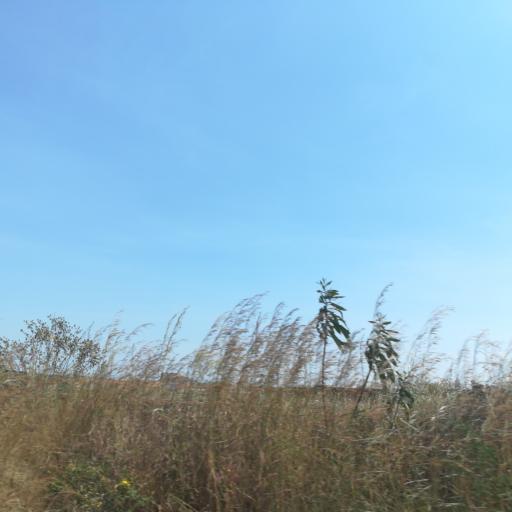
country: NG
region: Plateau
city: Bukuru
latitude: 9.8463
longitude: 8.9144
